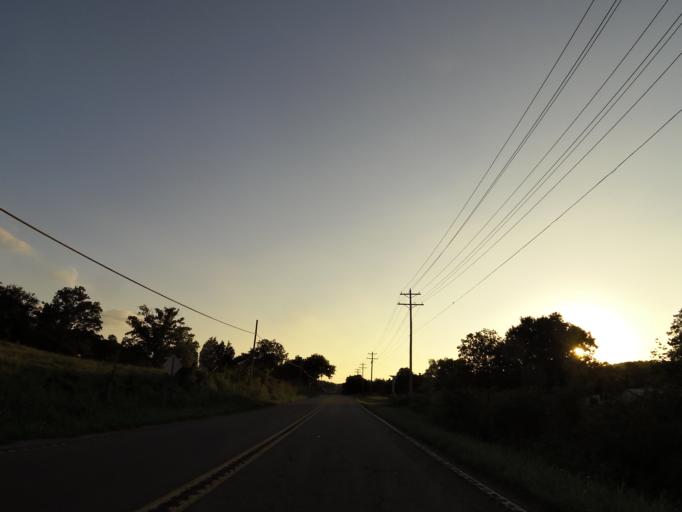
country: US
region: Tennessee
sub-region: Jefferson County
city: New Market
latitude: 36.0219
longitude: -83.5393
